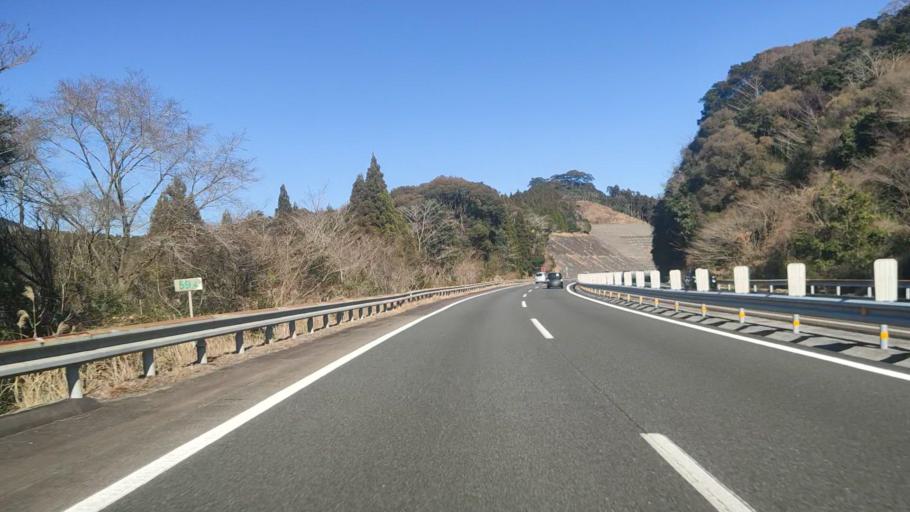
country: JP
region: Miyazaki
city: Miyakonojo
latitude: 31.8188
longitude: 131.2169
